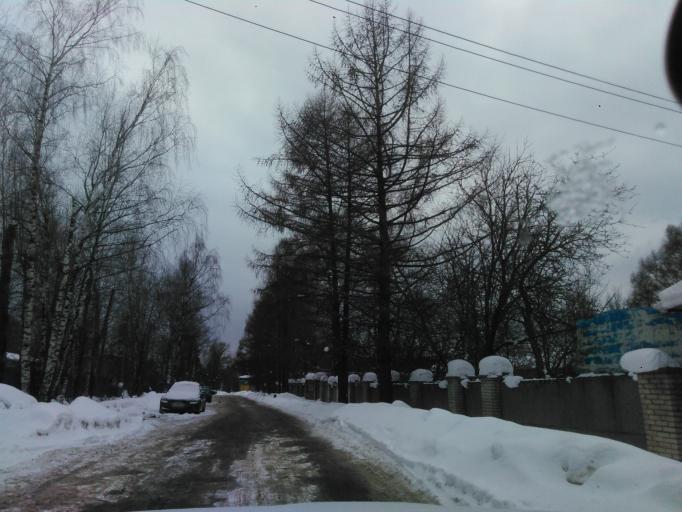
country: RU
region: Moskovskaya
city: Andreyevka
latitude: 55.9763
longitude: 37.1331
